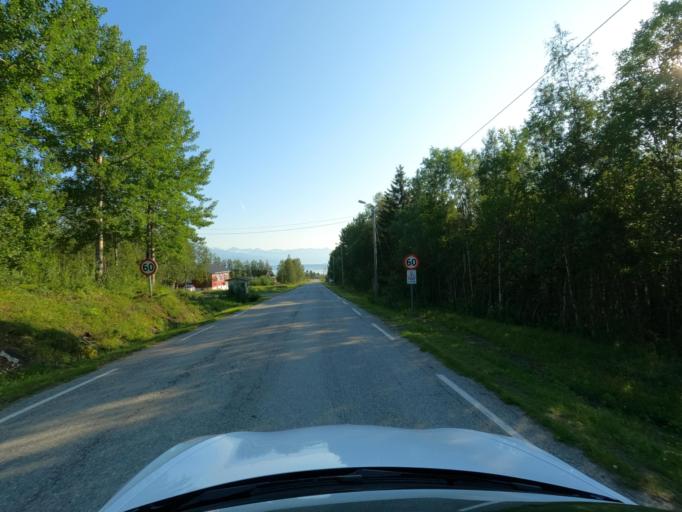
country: NO
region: Nordland
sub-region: Narvik
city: Bjerkvik
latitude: 68.5357
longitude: 17.4822
